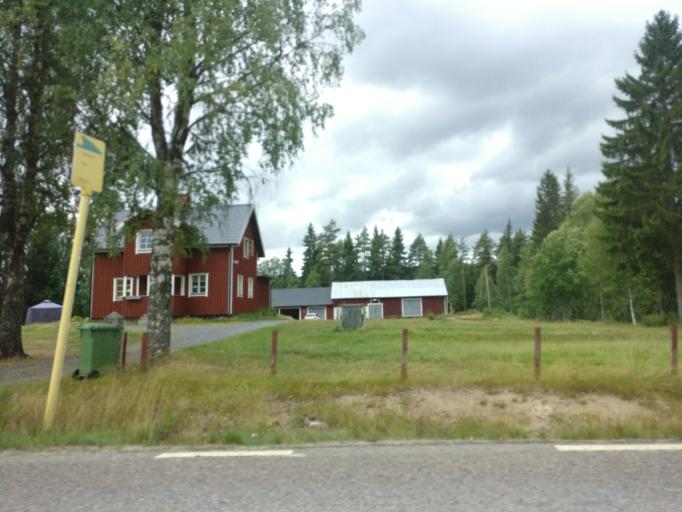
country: SE
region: Vaermland
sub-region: Torsby Kommun
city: Torsby
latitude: 60.7651
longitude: 12.7604
